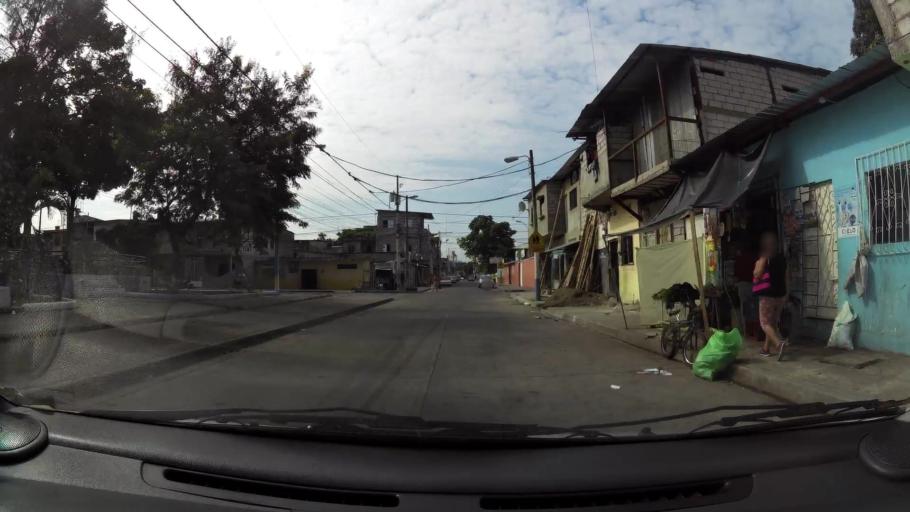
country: EC
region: Guayas
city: Guayaquil
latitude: -2.2555
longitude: -79.8743
